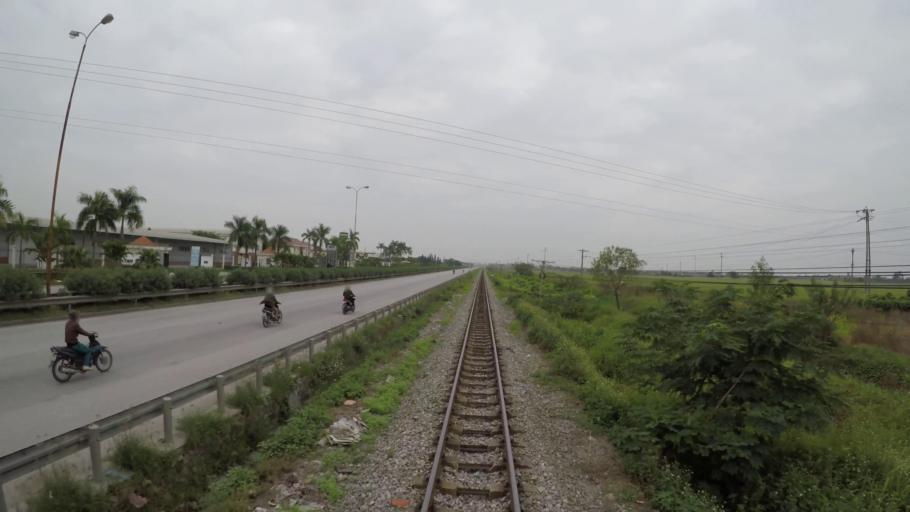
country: VN
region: Hai Duong
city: Phu Thai
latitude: 20.9655
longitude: 106.5133
